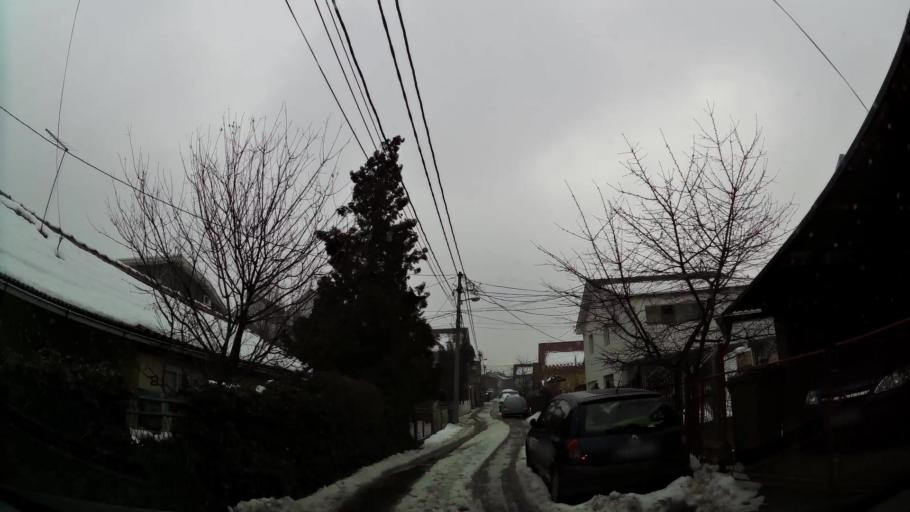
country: RS
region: Central Serbia
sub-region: Belgrade
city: Zvezdara
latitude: 44.7786
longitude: 20.5143
